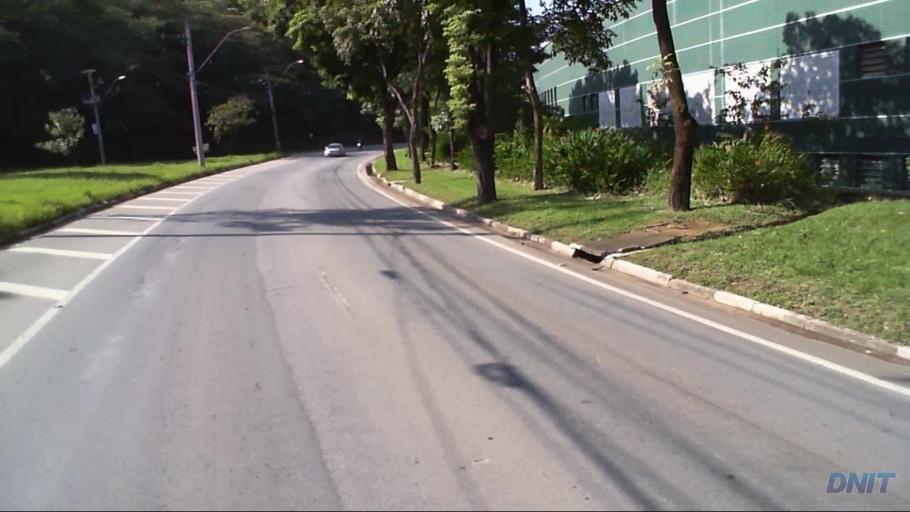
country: BR
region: Minas Gerais
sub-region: Ipatinga
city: Ipatinga
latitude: -19.4968
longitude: -42.5674
